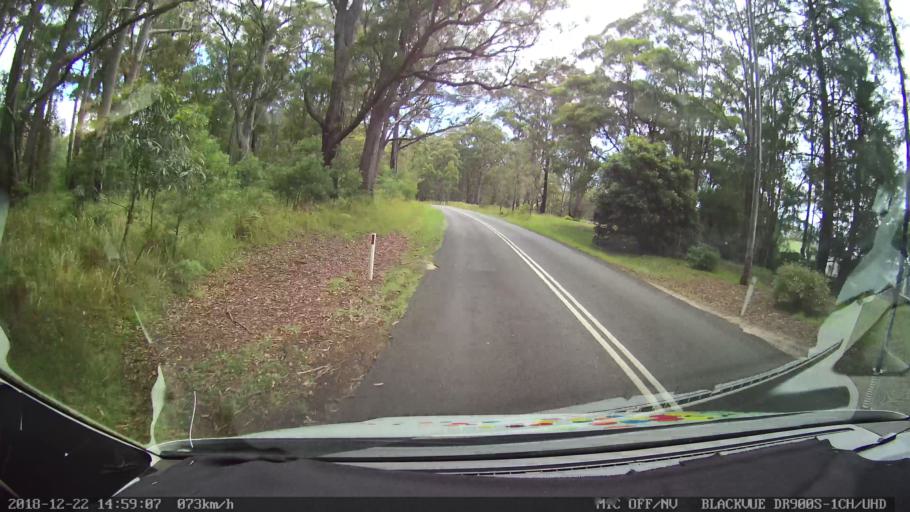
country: AU
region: New South Wales
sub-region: Bellingen
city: Dorrigo
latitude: -30.2443
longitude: 152.4843
